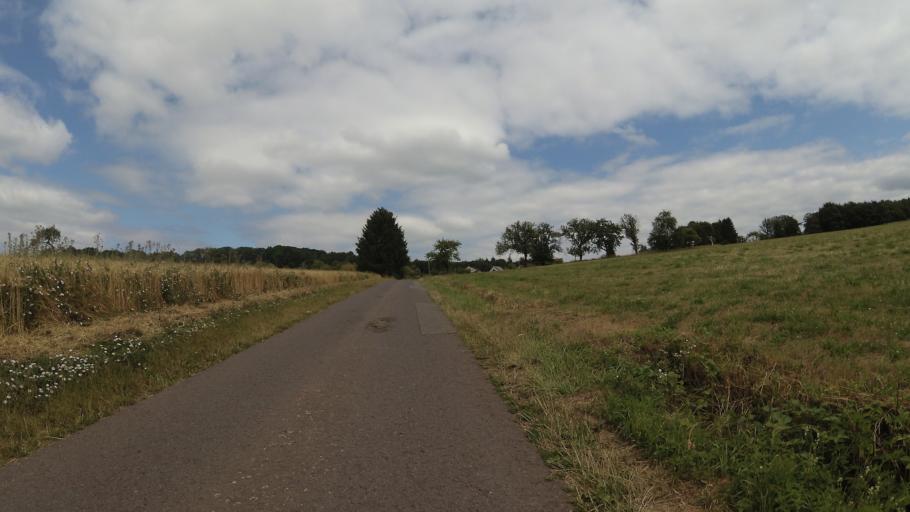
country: DE
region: Saarland
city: Mainzweiler
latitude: 49.4342
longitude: 7.0935
